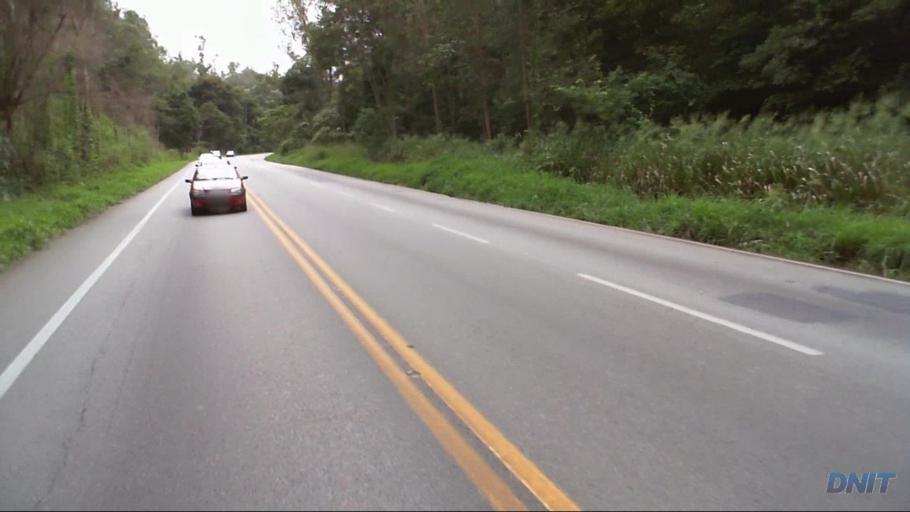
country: BR
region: Minas Gerais
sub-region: Joao Monlevade
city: Joao Monlevade
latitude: -19.8468
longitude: -43.1086
